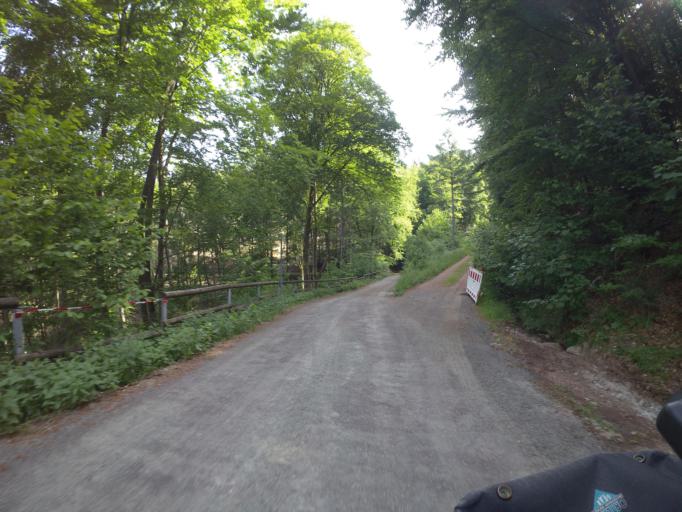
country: DE
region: Saarland
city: Nonnweiler
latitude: 49.6257
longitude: 6.9394
